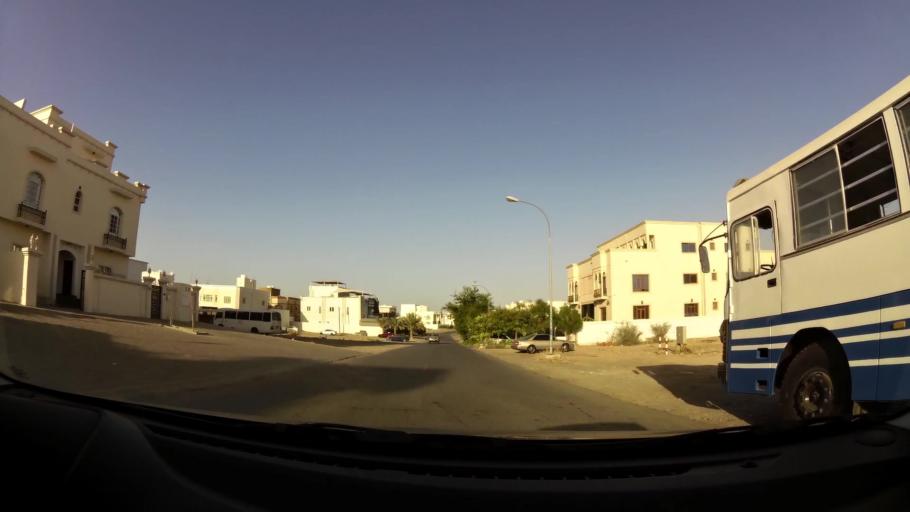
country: OM
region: Muhafazat Masqat
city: As Sib al Jadidah
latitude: 23.6095
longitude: 58.2283
